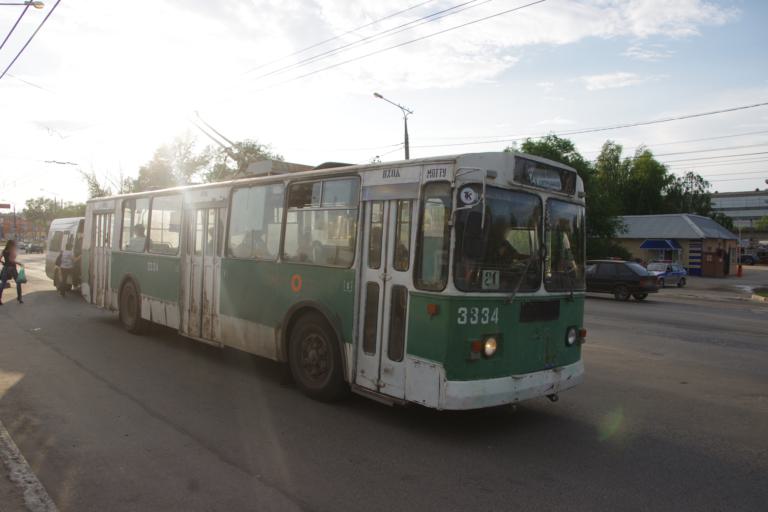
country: RU
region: Samara
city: Zhigulevsk
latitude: 53.4864
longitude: 49.4898
